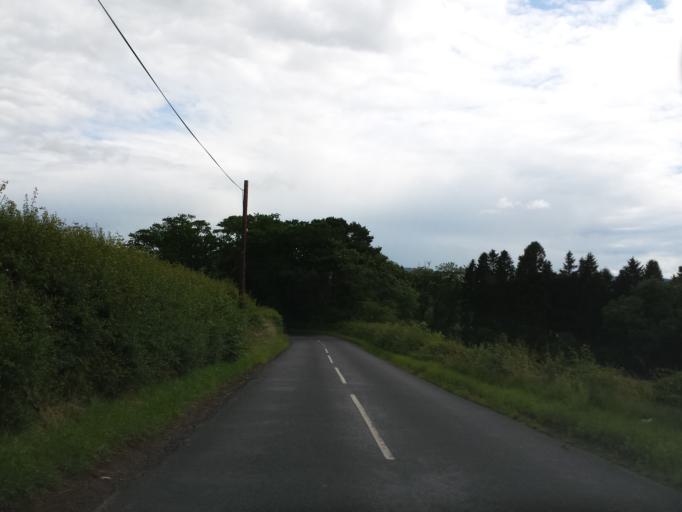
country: GB
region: Scotland
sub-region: The Scottish Borders
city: Saint Boswells
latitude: 55.5857
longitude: -2.6251
